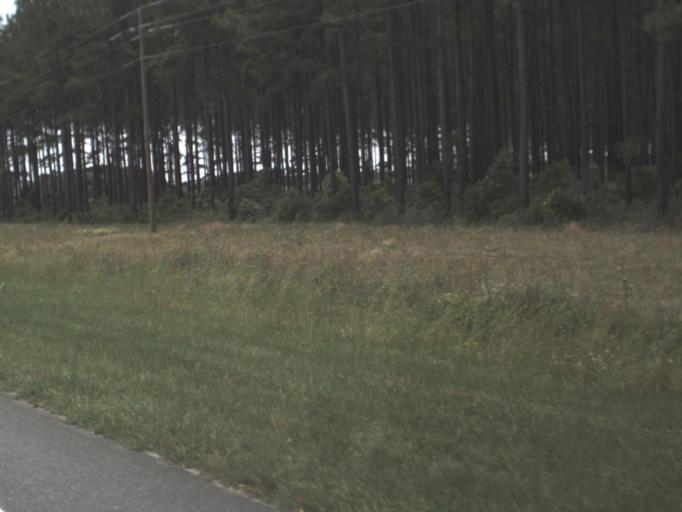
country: US
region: Florida
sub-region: Gulf County
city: Wewahitchka
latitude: 30.2184
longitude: -85.2049
